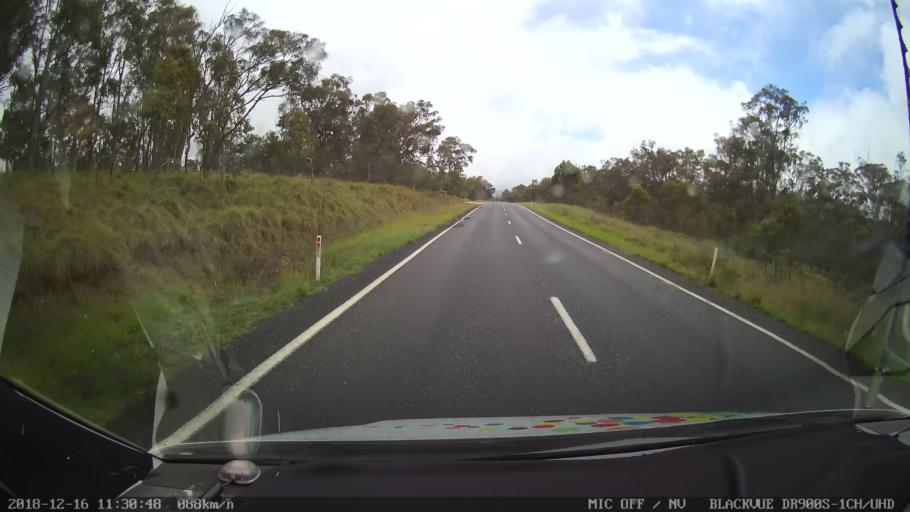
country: AU
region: New South Wales
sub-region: Tenterfield Municipality
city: Carrolls Creek
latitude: -29.0280
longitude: 152.1222
